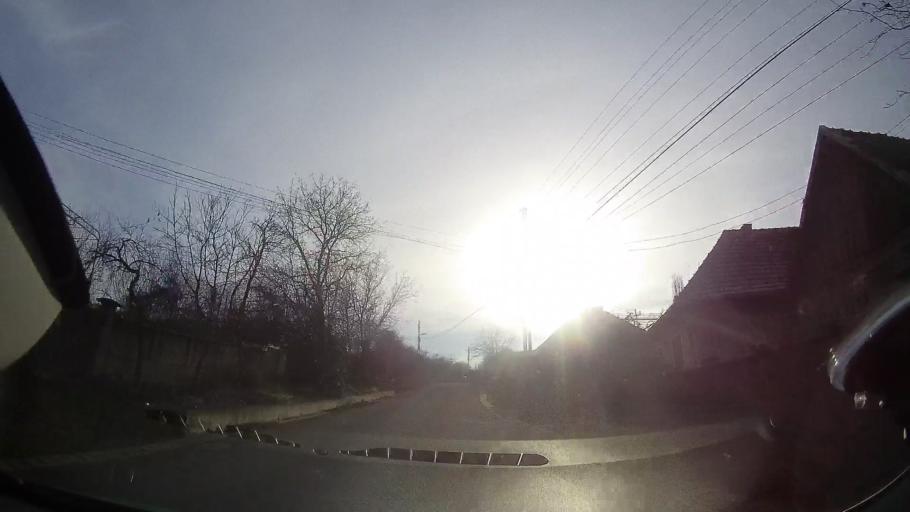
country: RO
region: Bihor
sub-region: Comuna Sarbi
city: Burzuc
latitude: 47.1439
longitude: 22.1857
